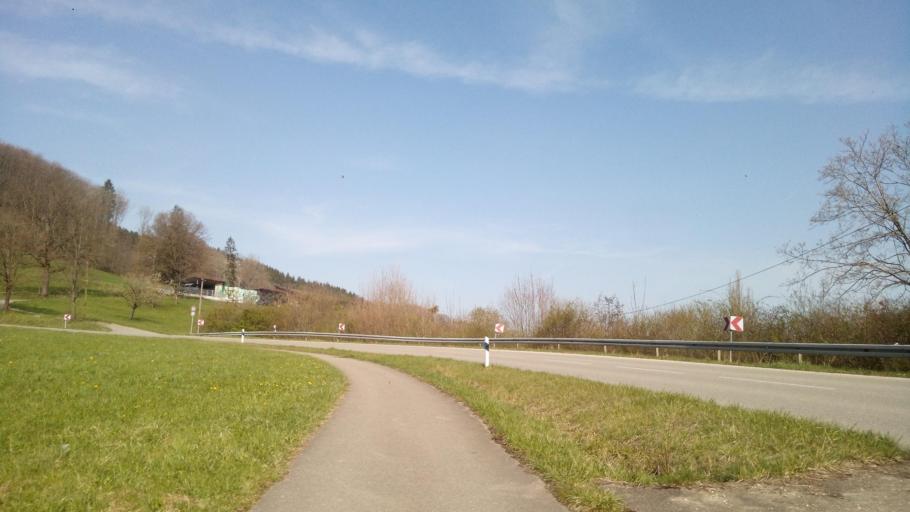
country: DE
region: Baden-Wuerttemberg
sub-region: Regierungsbezirk Stuttgart
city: Donzdorf
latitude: 48.7130
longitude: 9.8163
